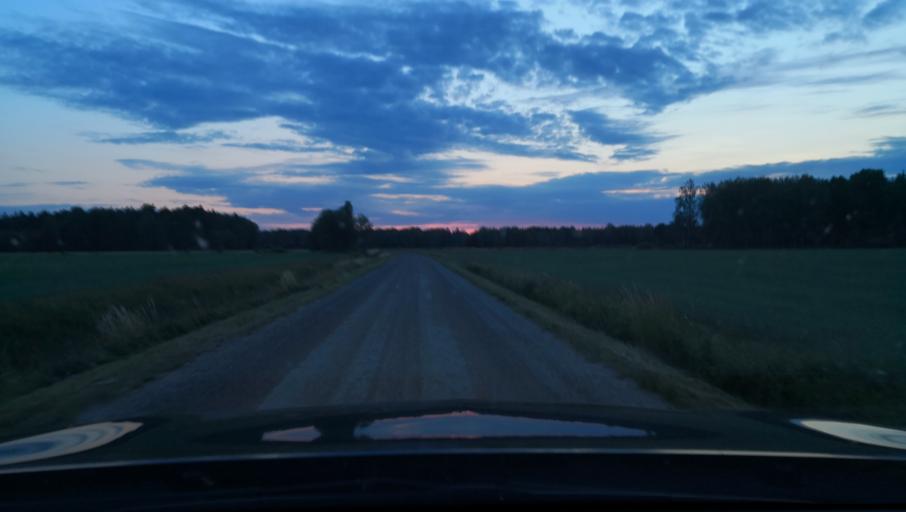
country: SE
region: Uppsala
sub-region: Heby Kommun
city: OEstervala
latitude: 60.0132
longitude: 17.3094
